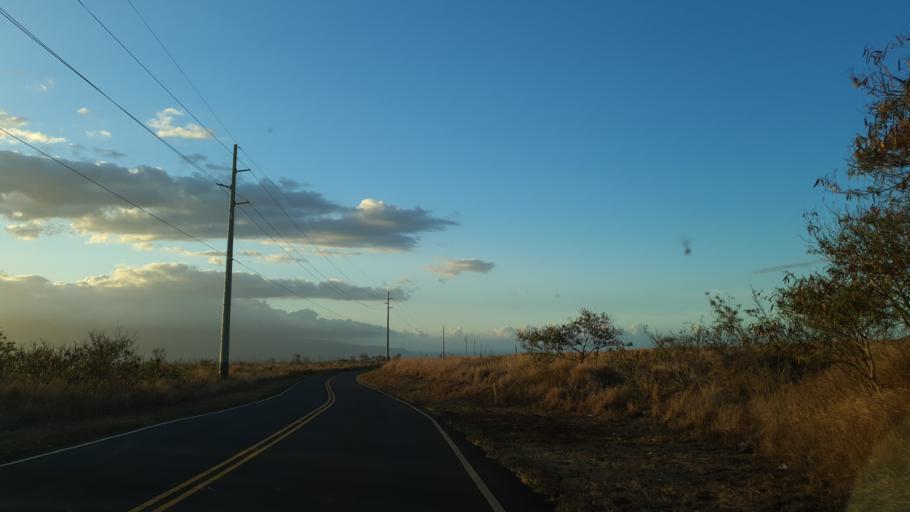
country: US
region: Hawaii
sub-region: Maui County
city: Pukalani
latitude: 20.8036
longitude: -156.3774
